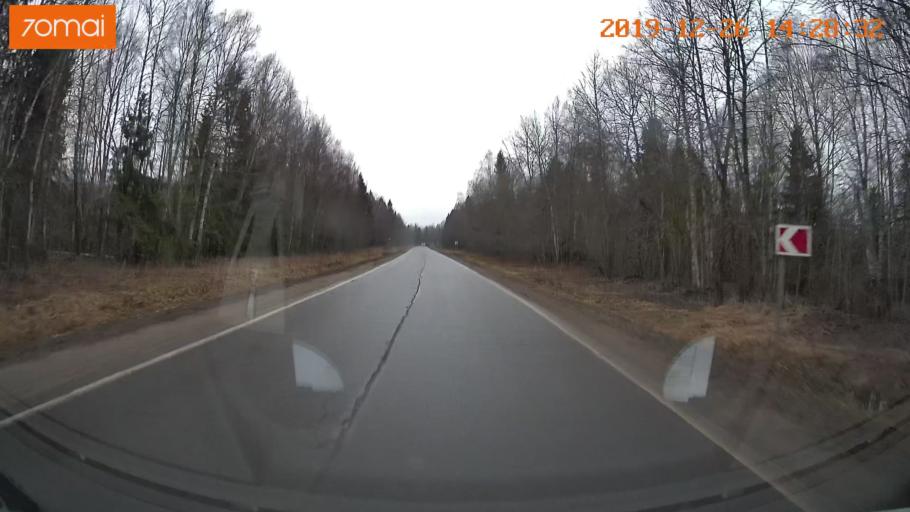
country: RU
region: Jaroslavl
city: Poshekhon'ye
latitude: 58.4745
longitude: 39.0521
